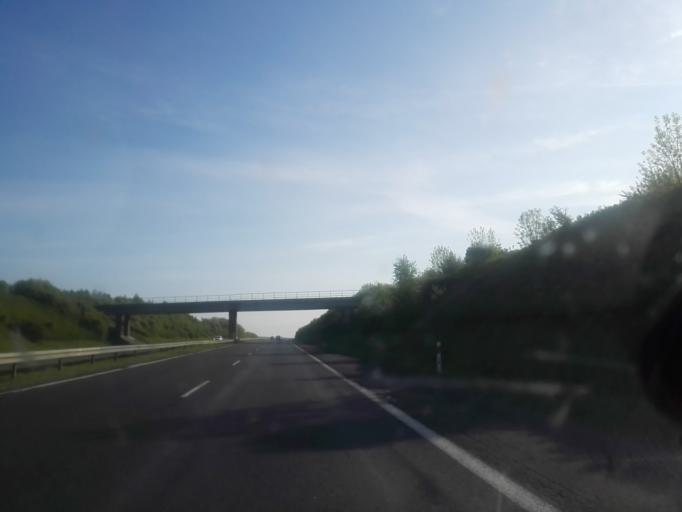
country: PL
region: Lodz Voivodeship
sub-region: Powiat radomszczanski
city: Radomsko
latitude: 51.1384
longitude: 19.4226
